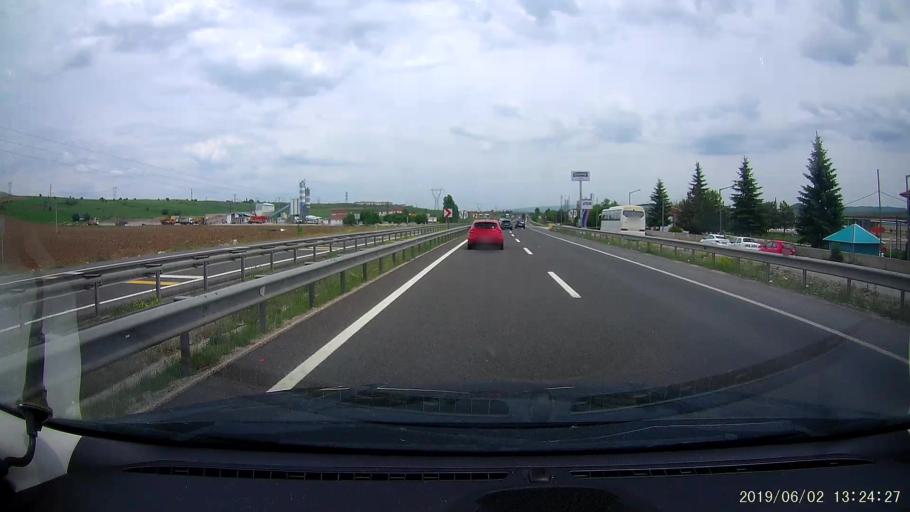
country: TR
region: Cankiri
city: Cerkes
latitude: 40.8239
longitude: 32.8465
